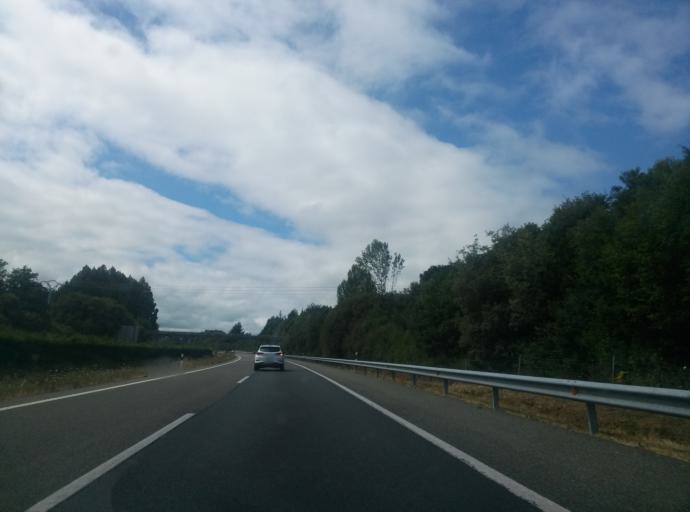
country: ES
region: Galicia
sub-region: Provincia de Lugo
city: Rabade
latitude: 43.1362
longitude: -7.6377
